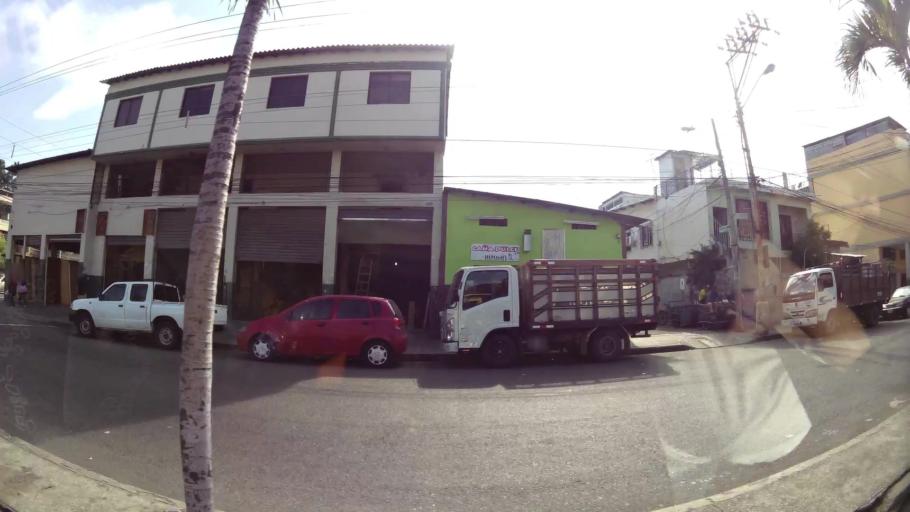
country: EC
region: Guayas
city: Guayaquil
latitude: -2.2036
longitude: -79.9110
